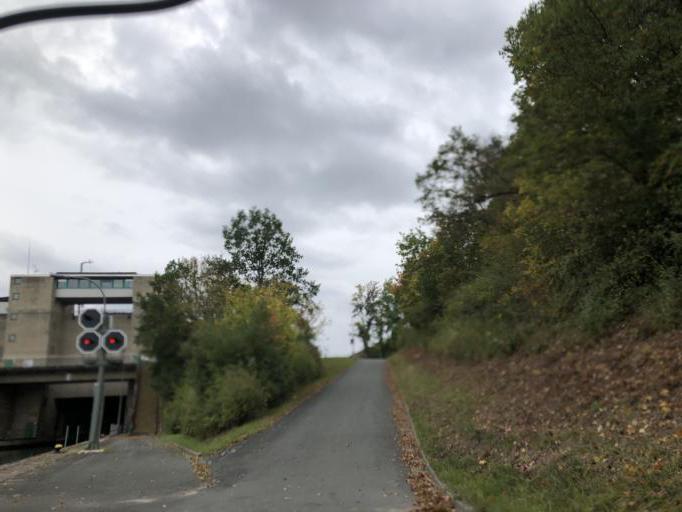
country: DE
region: Bavaria
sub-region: Regierungsbezirk Mittelfranken
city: Erlangen
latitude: 49.5573
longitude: 10.9695
